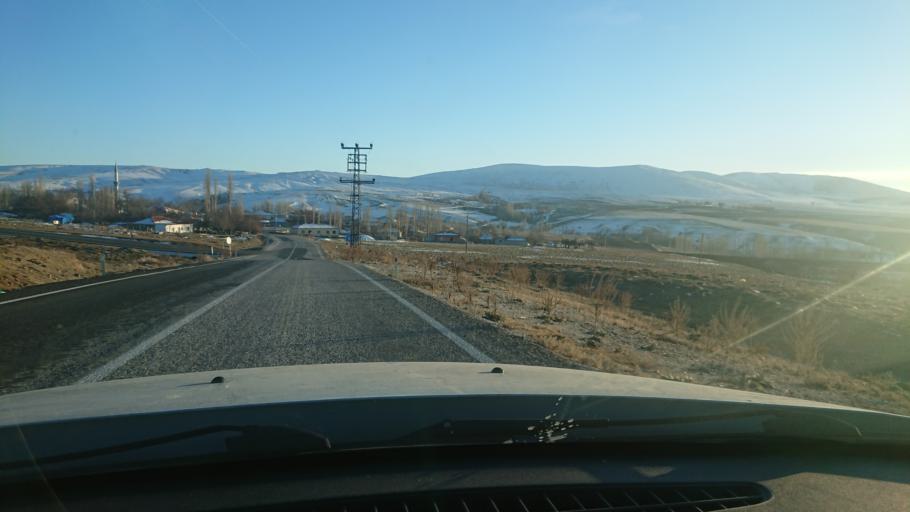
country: TR
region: Aksaray
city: Ortakoy
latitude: 38.7592
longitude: 33.9335
